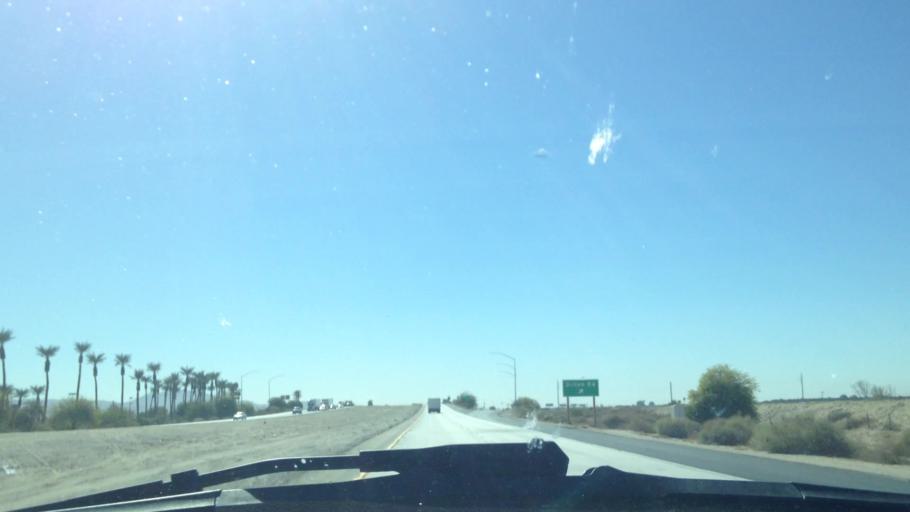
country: US
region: California
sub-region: Riverside County
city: Indio
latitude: 33.7122
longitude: -116.1868
